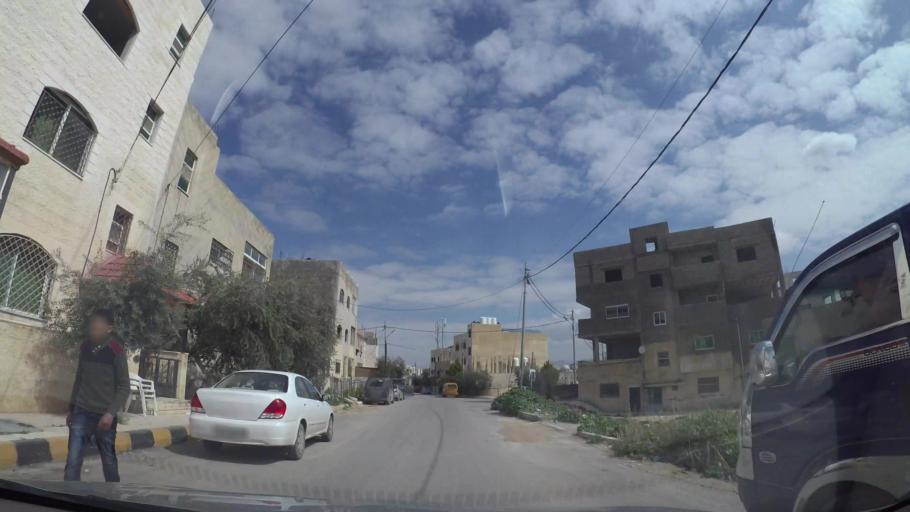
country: JO
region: Amman
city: Al Jubayhah
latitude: 32.0685
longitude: 35.8178
